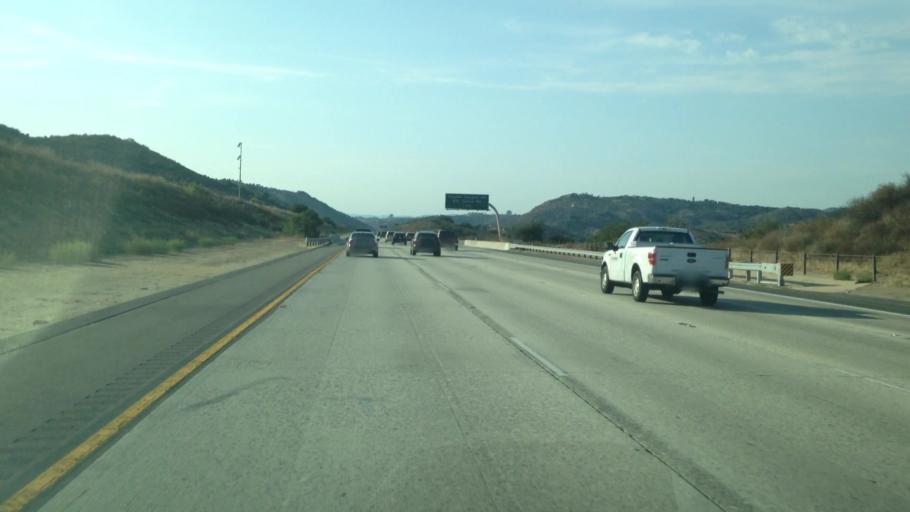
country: US
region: California
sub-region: San Diego County
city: Hidden Meadows
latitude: 33.2313
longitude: -117.1464
